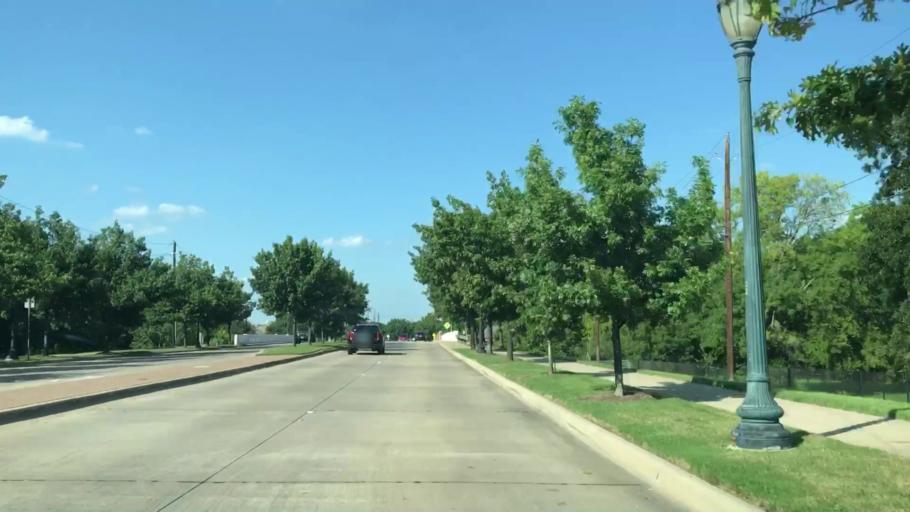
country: US
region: Texas
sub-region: Tarrant County
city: Keller
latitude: 32.9275
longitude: -97.2202
